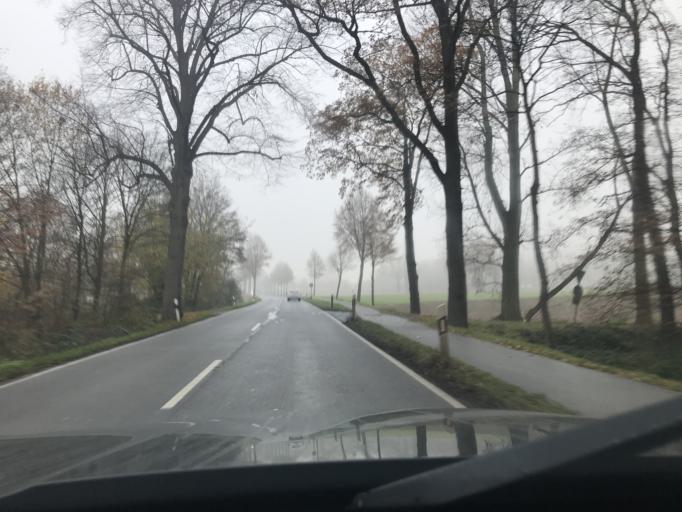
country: DE
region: North Rhine-Westphalia
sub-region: Regierungsbezirk Dusseldorf
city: Nettetal
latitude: 51.2830
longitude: 6.2670
